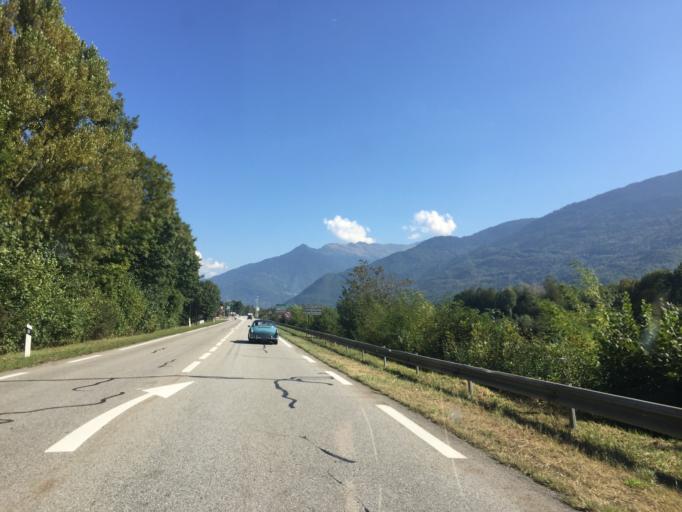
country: FR
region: Rhone-Alpes
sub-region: Departement de la Savoie
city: Frontenex
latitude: 45.6240
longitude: 6.3156
